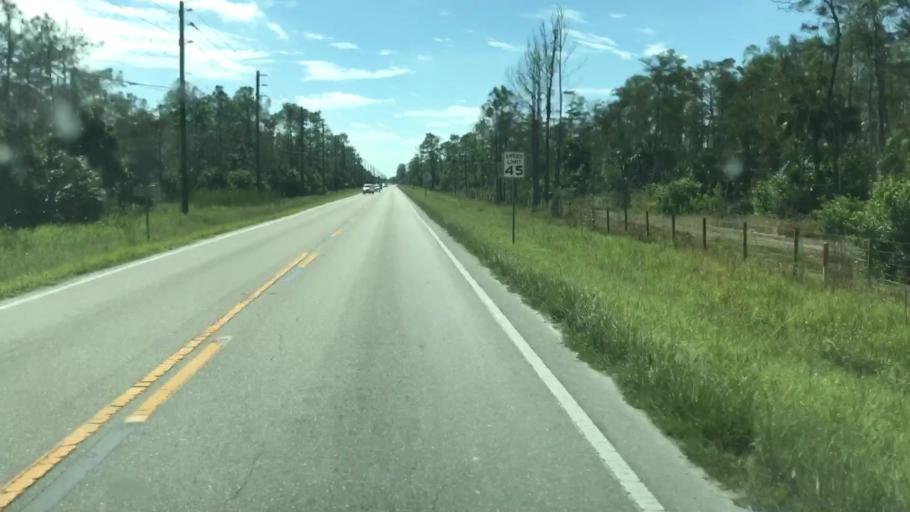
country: US
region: Florida
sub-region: Lee County
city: Bonita Springs
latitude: 26.3448
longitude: -81.7387
